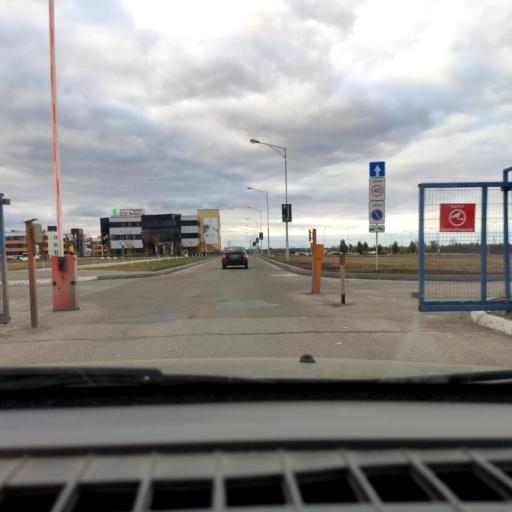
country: RU
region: Samara
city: Podstepki
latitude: 53.5589
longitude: 49.2149
